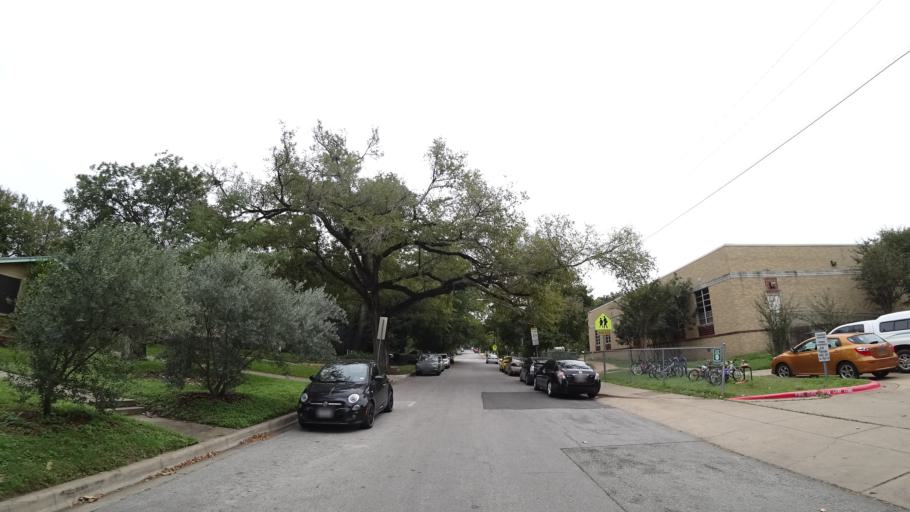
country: US
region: Texas
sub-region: Travis County
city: Austin
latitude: 30.2942
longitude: -97.7275
